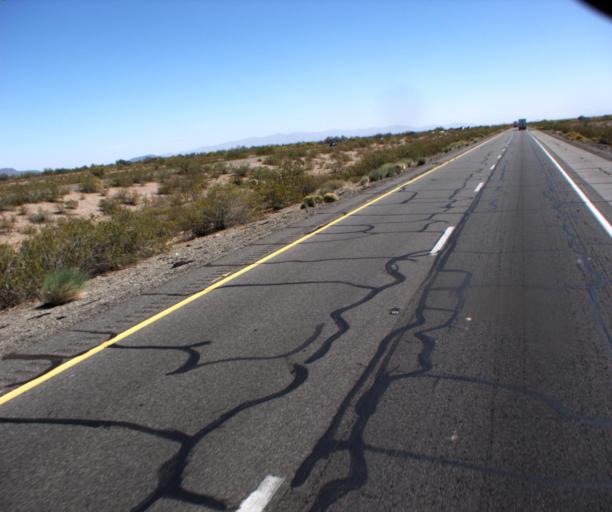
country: US
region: Arizona
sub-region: Maricopa County
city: Buckeye
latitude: 33.5100
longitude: -113.0091
